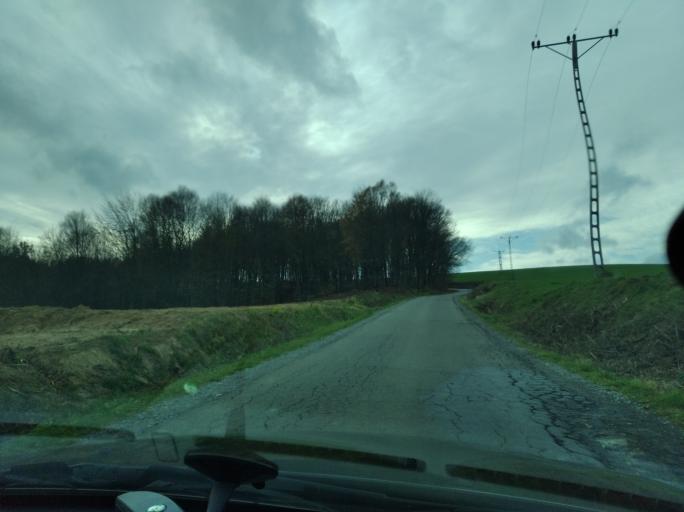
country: PL
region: Subcarpathian Voivodeship
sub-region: Powiat strzyzowski
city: Strzyzow
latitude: 49.9212
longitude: 21.7667
